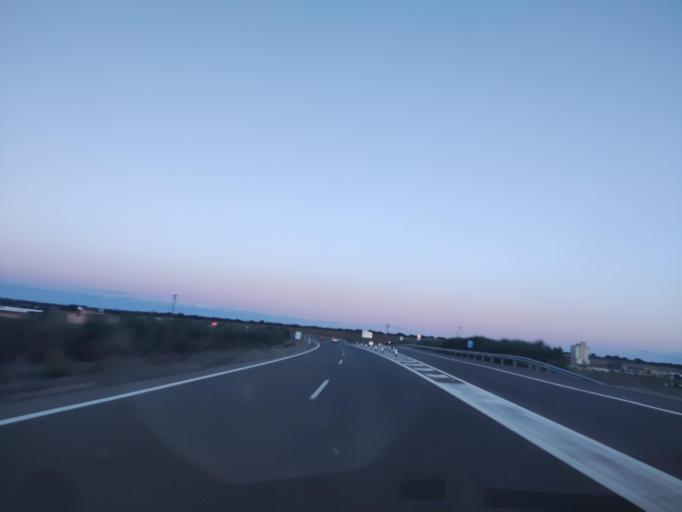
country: ES
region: Castille and Leon
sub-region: Provincia de Salamanca
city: Aldehuela de la Boveda
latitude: 40.8473
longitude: -6.0551
